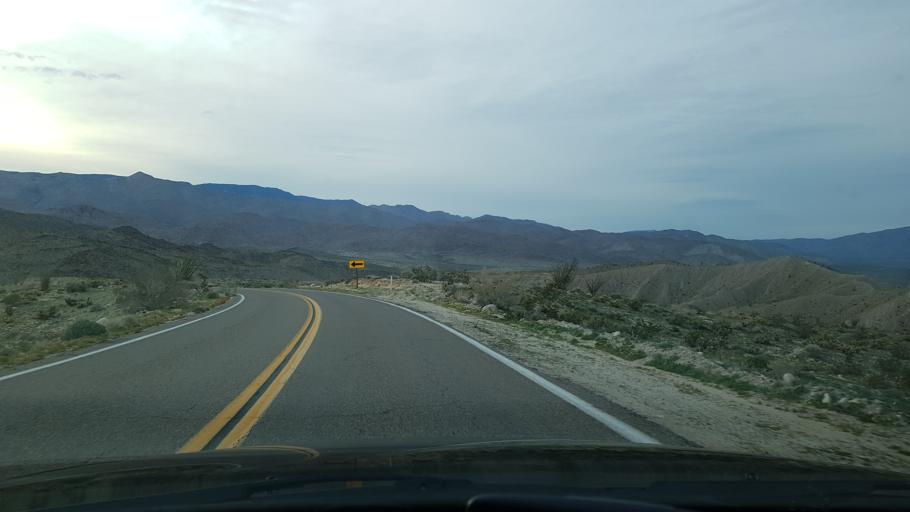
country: US
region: California
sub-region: San Diego County
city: Pine Valley
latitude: 32.8314
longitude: -116.1751
